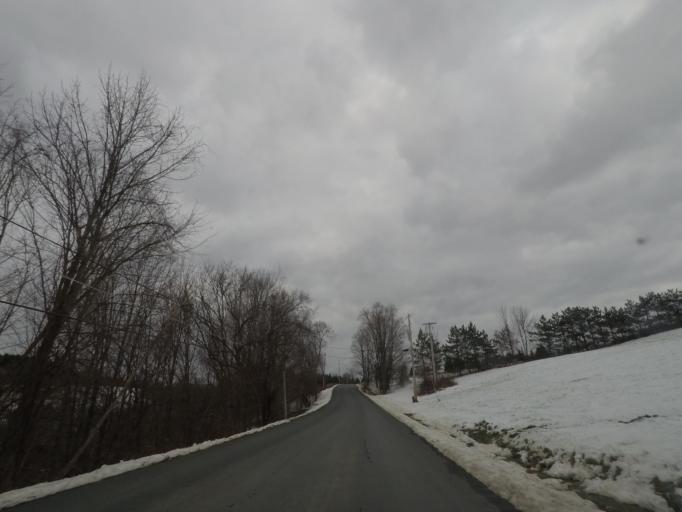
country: US
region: New York
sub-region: Rensselaer County
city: West Sand Lake
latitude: 42.5945
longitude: -73.6308
